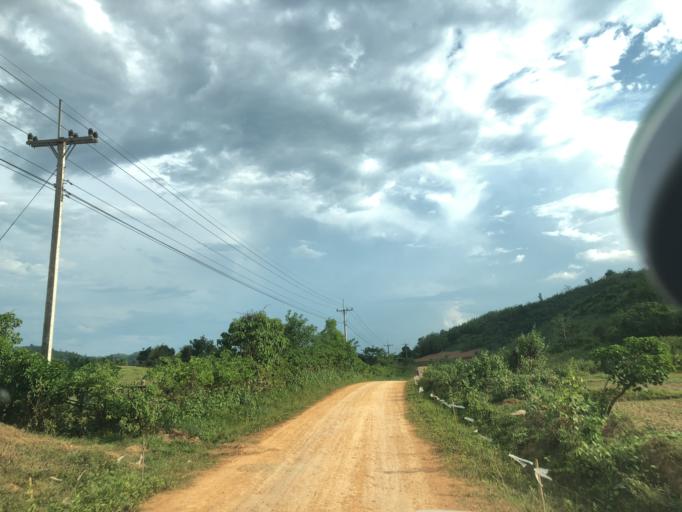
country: TH
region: Loei
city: Chiang Khan
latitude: 18.0002
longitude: 101.4198
